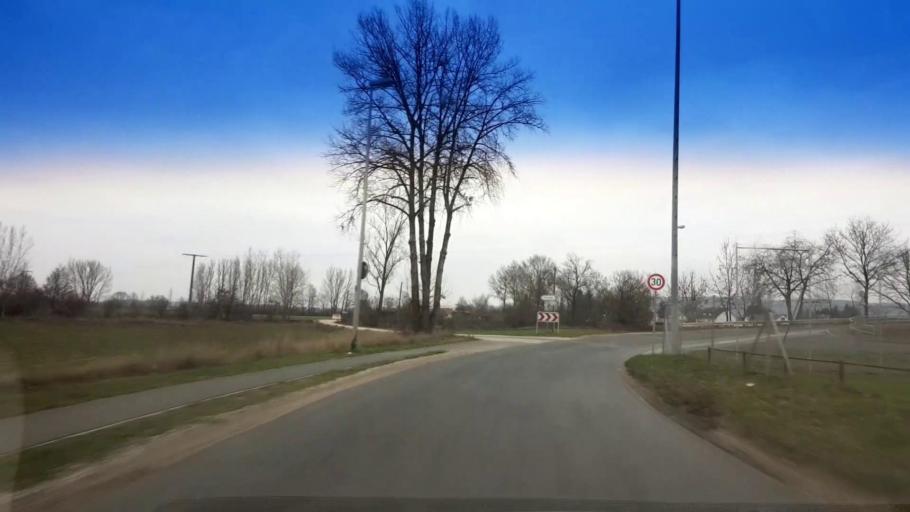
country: DE
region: Bavaria
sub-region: Upper Franconia
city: Altendorf
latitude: 49.7938
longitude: 11.0049
